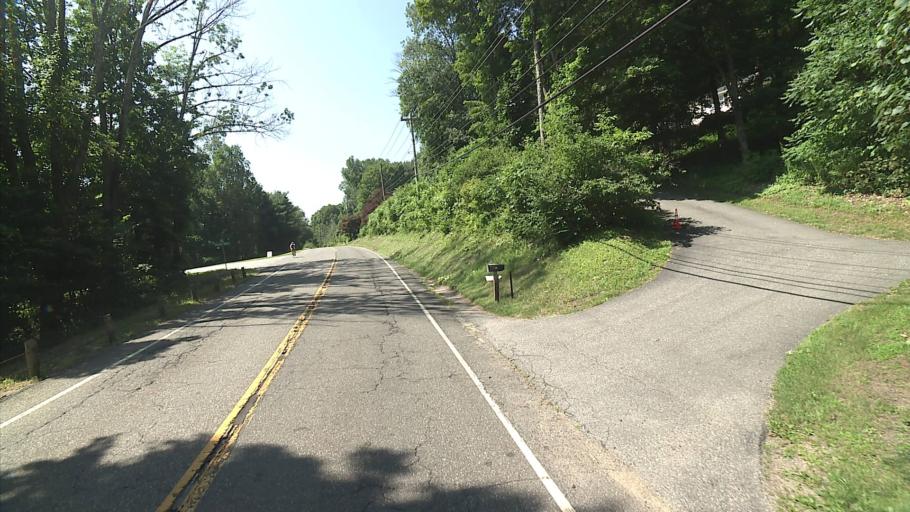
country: US
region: Connecticut
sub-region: Litchfield County
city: New Preston
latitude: 41.7205
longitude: -73.3430
